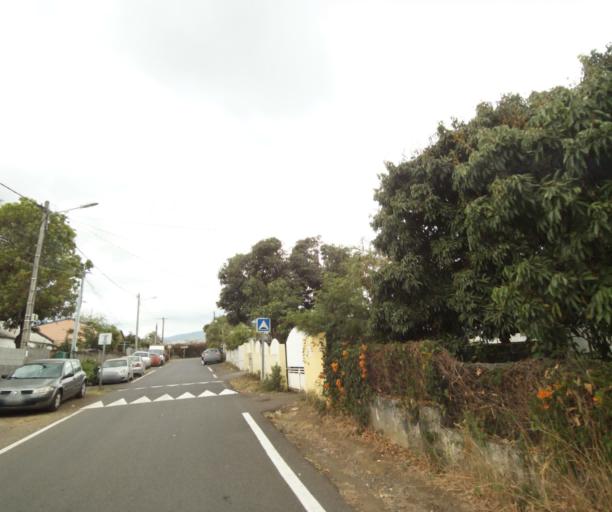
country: RE
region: Reunion
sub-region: Reunion
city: Saint-Paul
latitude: -20.9871
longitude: 55.2992
